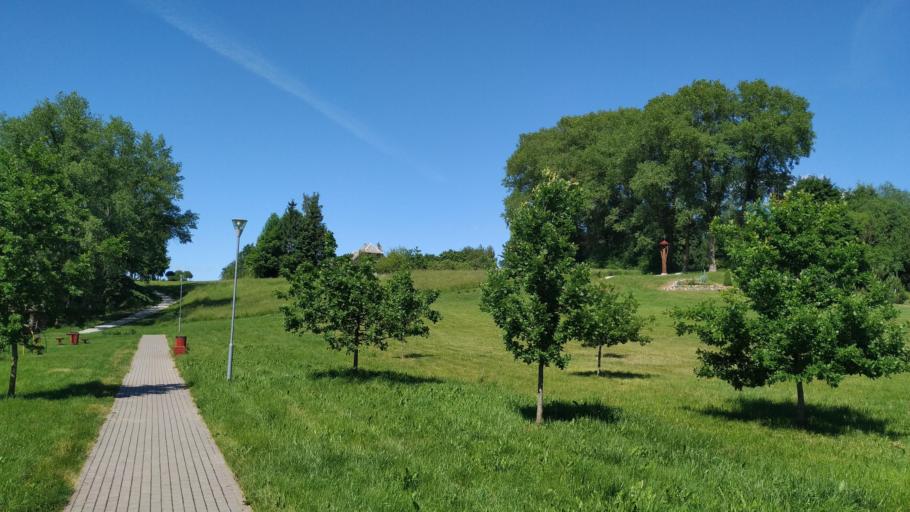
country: LT
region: Utenos apskritis
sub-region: Anyksciai
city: Anyksciai
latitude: 55.2953
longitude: 25.1157
